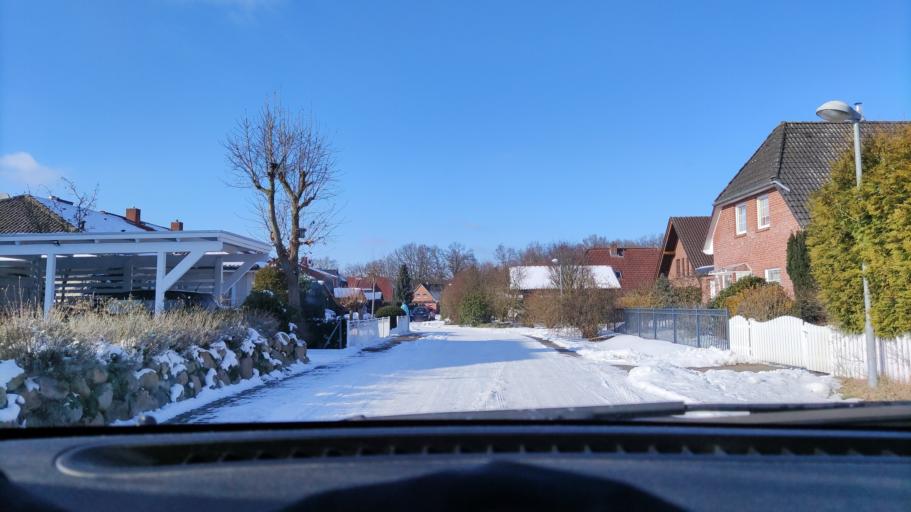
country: DE
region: Lower Saxony
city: Wendisch Evern
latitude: 53.2165
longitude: 10.4805
